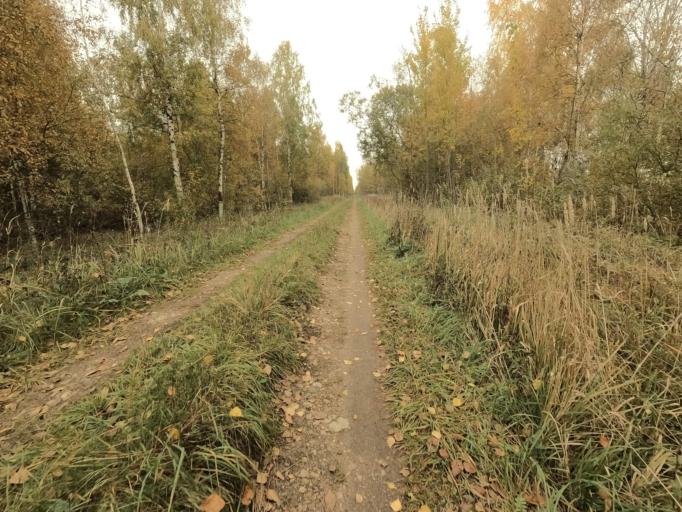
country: RU
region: Novgorod
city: Pankovka
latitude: 58.8858
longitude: 30.9465
